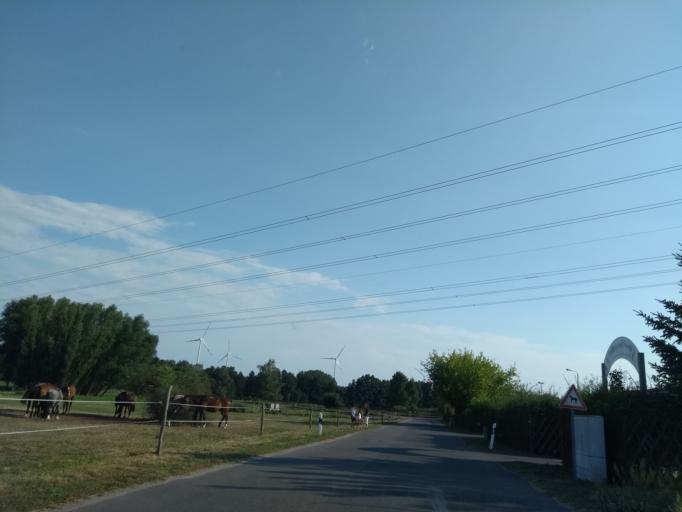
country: DE
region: Brandenburg
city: Lubbenau
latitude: 51.8348
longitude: 13.9501
